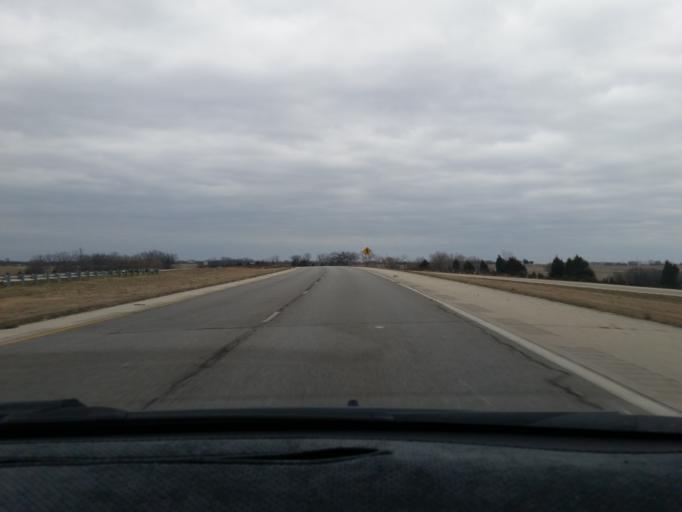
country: US
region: Kansas
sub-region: Douglas County
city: Eudora
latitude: 38.9447
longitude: -95.0373
